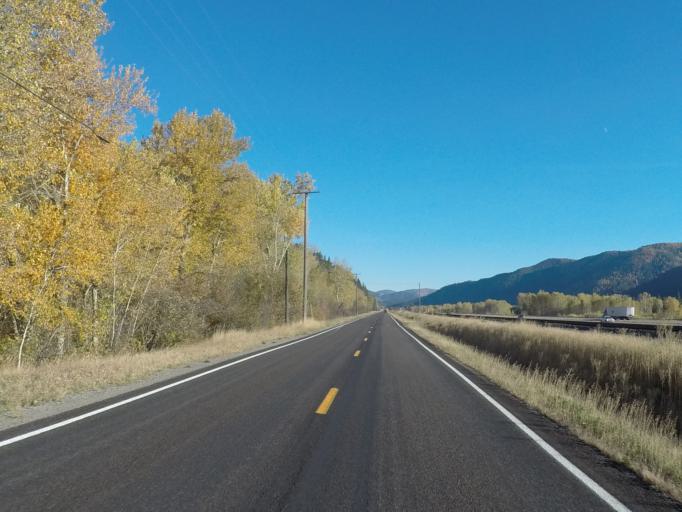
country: US
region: Montana
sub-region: Missoula County
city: Bonner-West Riverside
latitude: 46.8219
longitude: -113.8029
